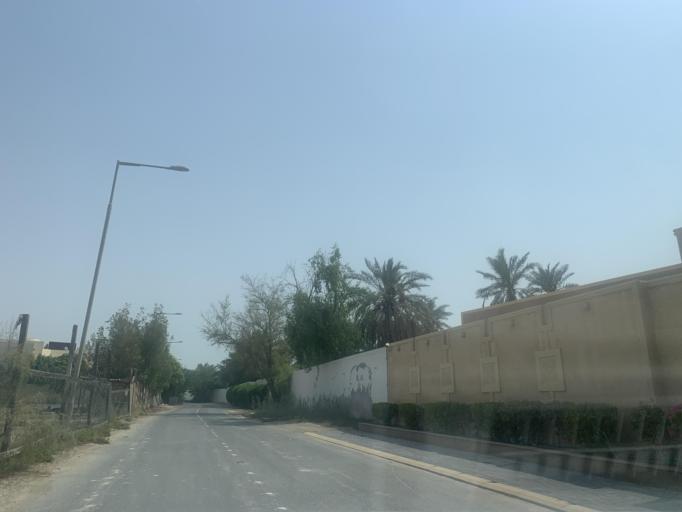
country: BH
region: Central Governorate
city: Madinat Hamad
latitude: 26.1708
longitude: 50.4534
